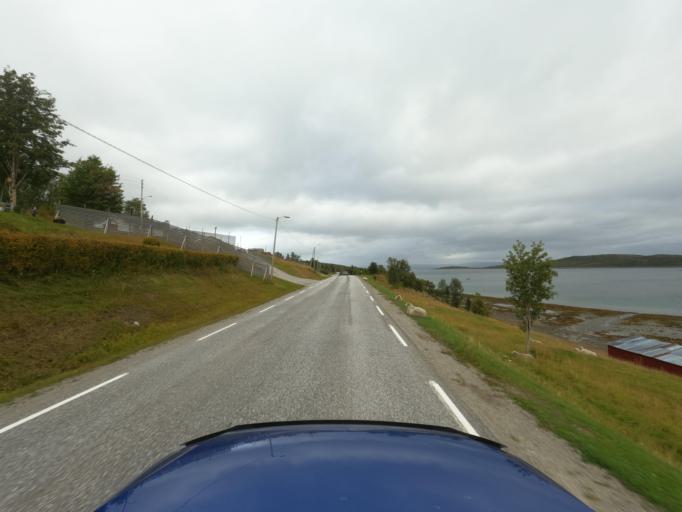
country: NO
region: Finnmark Fylke
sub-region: Porsanger
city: Lakselv
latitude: 70.3585
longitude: 25.0488
